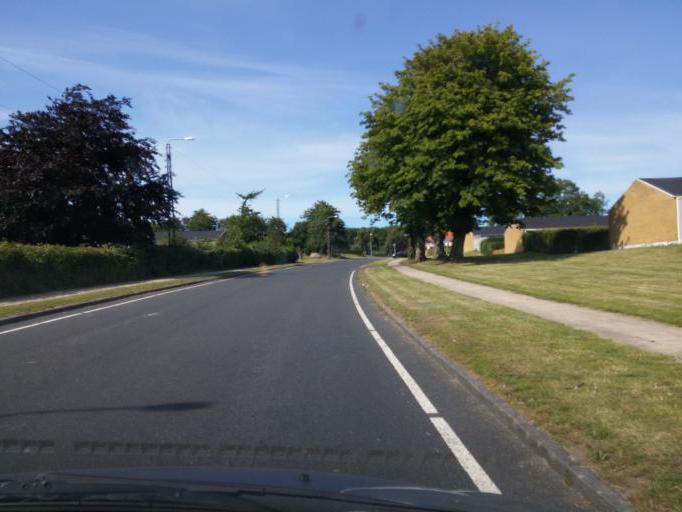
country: DK
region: South Denmark
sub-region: Kerteminde Kommune
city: Munkebo
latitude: 55.4642
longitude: 10.5631
